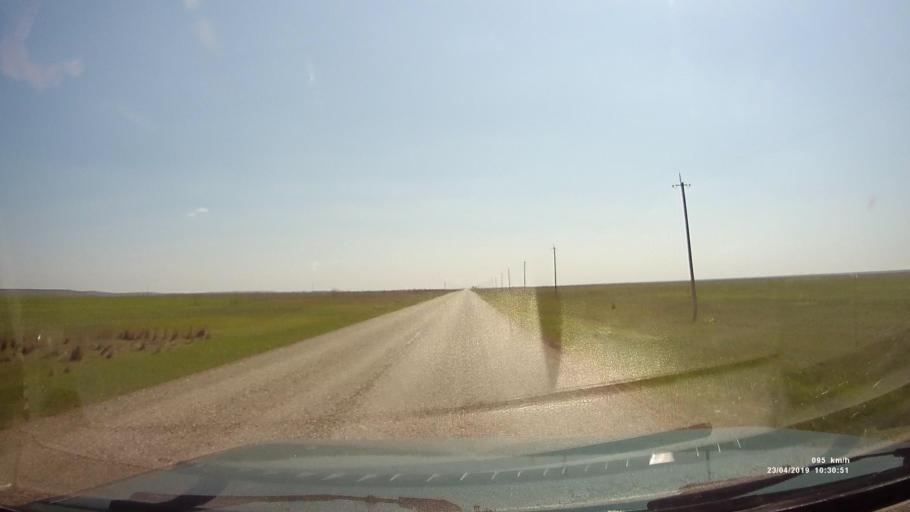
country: RU
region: Kalmykiya
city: Yashalta
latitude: 46.5894
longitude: 42.5520
